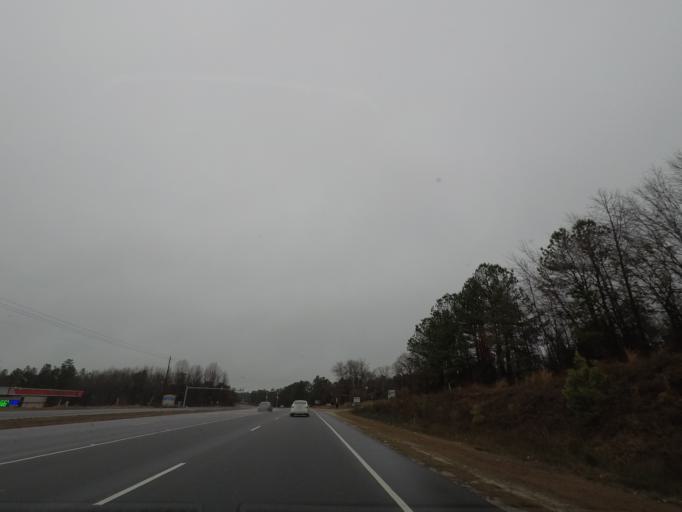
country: US
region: North Carolina
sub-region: Cumberland County
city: Spring Lake
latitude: 35.2452
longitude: -79.0227
